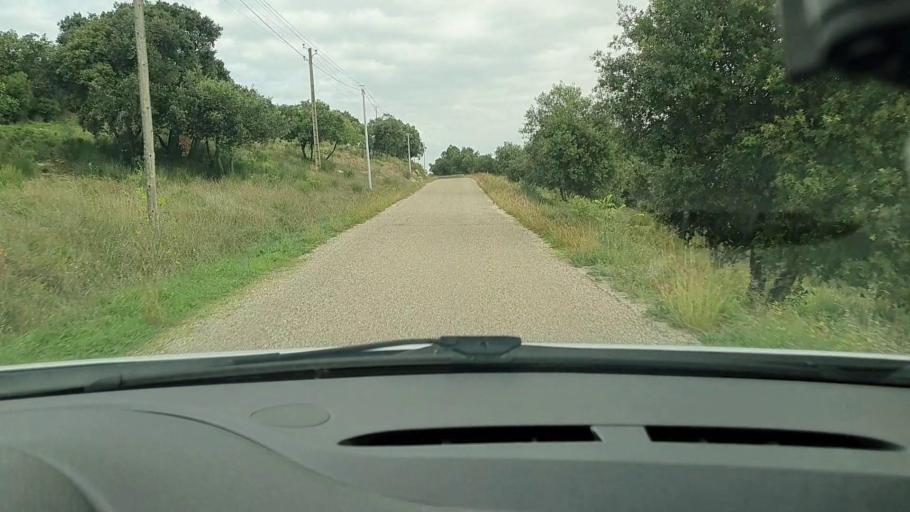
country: FR
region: Languedoc-Roussillon
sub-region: Departement du Gard
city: Montaren-et-Saint-Mediers
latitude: 44.1050
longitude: 4.3021
